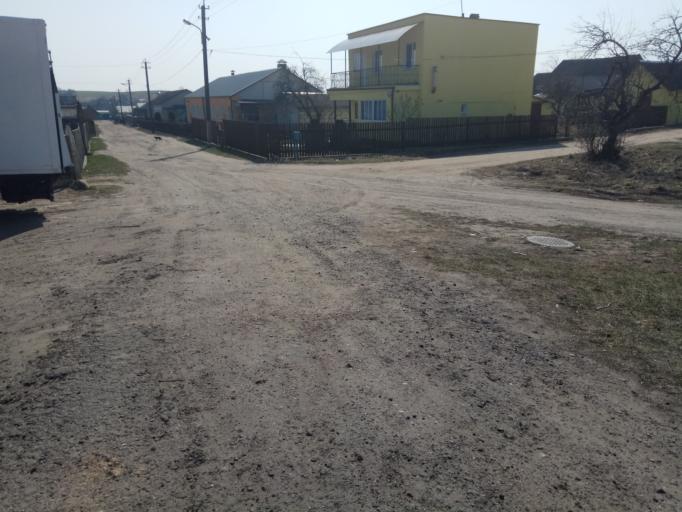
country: BY
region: Minsk
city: Valozhyn
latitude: 54.0820
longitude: 26.5170
